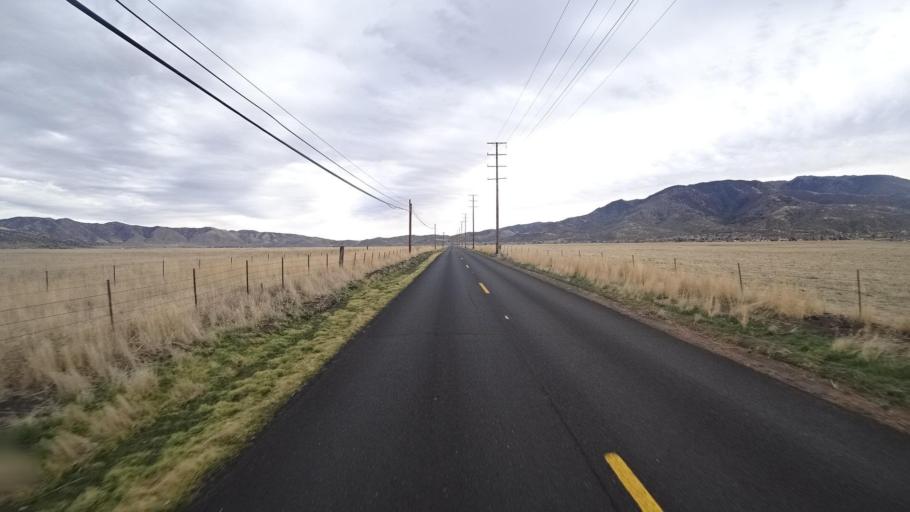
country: US
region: California
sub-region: Kern County
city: Stallion Springs
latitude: 35.0937
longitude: -118.6342
